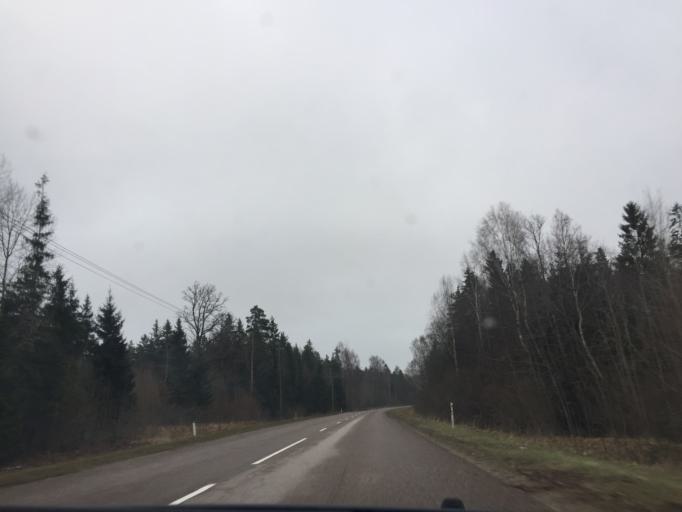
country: LV
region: Burtnieki
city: Matisi
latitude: 57.5149
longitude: 25.1542
